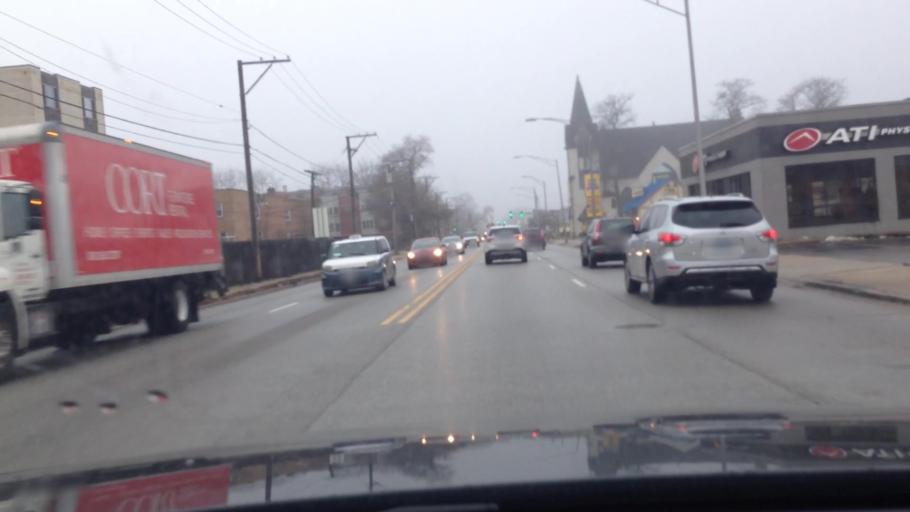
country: US
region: Illinois
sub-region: Cook County
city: Forest Park
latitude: 41.8854
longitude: -87.8049
